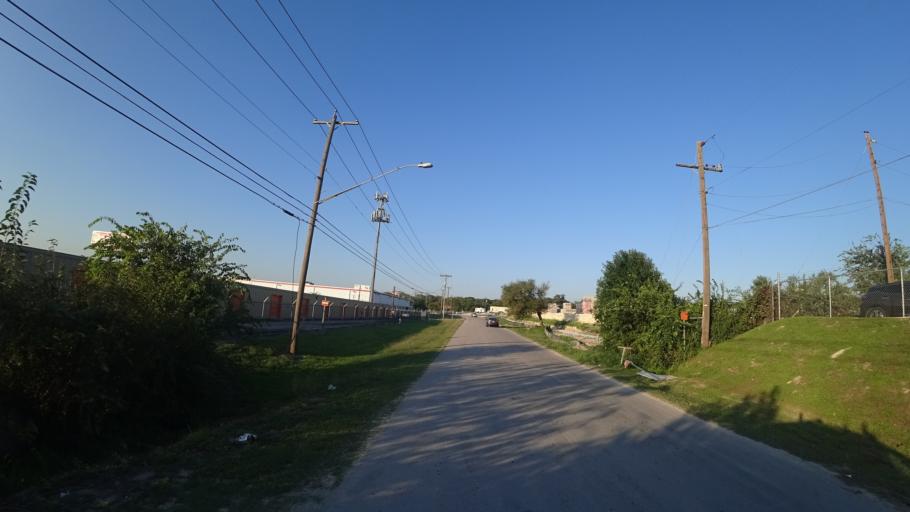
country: US
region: Texas
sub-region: Travis County
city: Wells Branch
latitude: 30.3638
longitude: -97.6825
